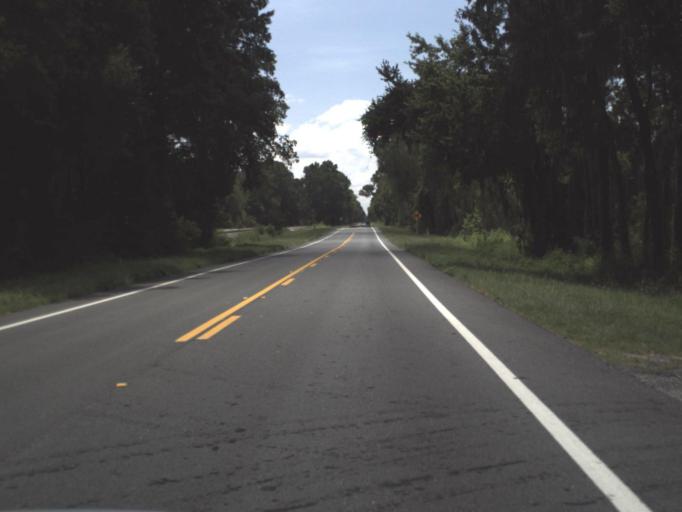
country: US
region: Florida
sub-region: Suwannee County
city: Wellborn
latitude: 30.3847
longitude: -82.8183
